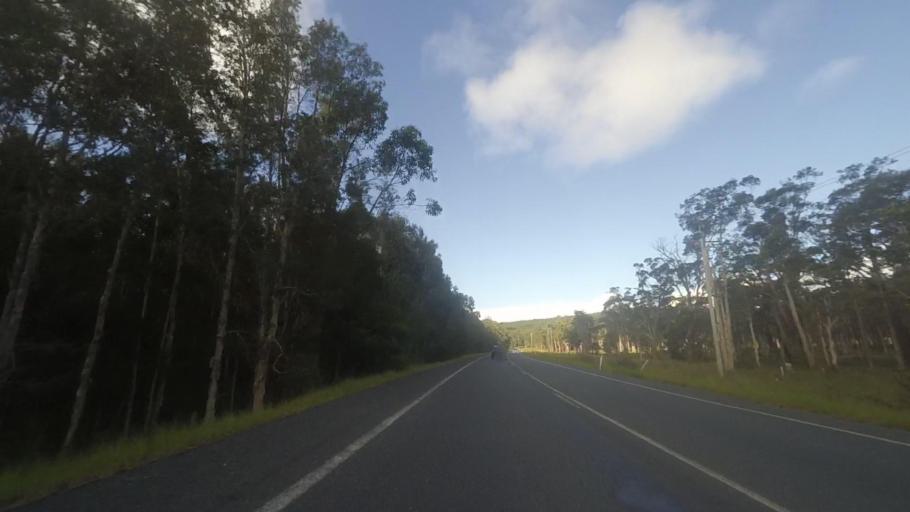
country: AU
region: New South Wales
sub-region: Great Lakes
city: Forster
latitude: -32.3539
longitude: 152.5070
